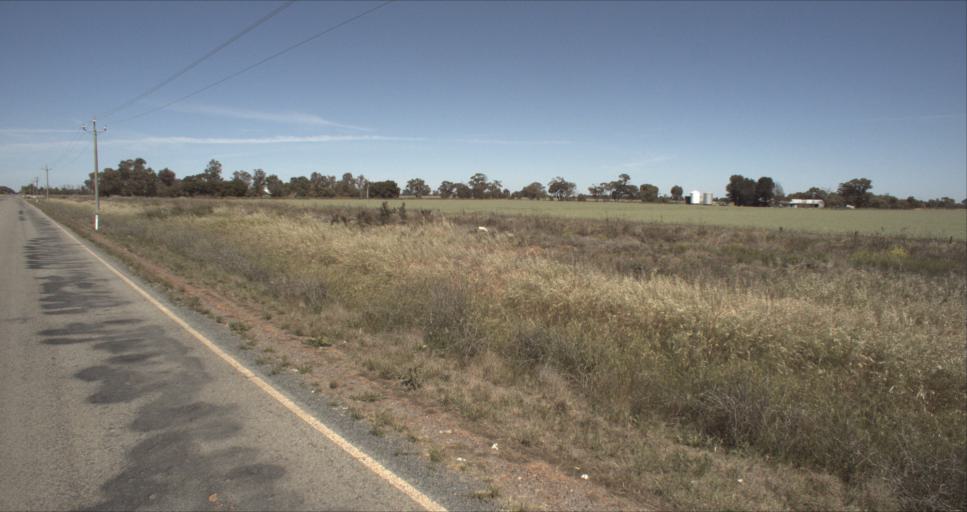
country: AU
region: New South Wales
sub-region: Leeton
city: Leeton
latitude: -34.5111
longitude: 146.2851
